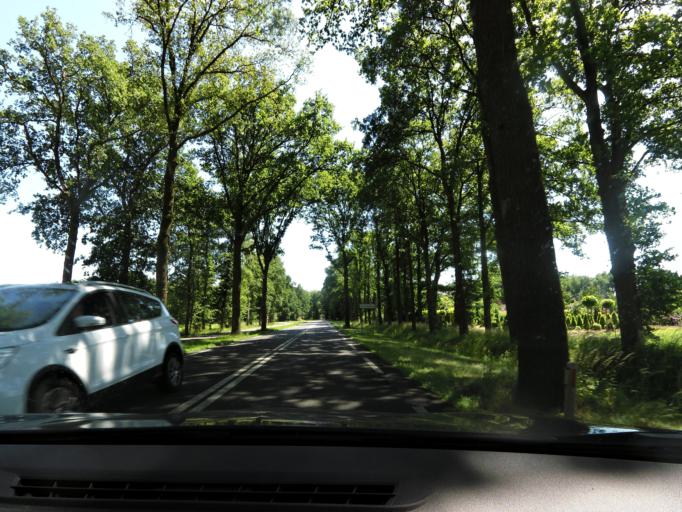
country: NL
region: Gelderland
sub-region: Berkelland
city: Neede
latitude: 52.1598
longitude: 6.6012
